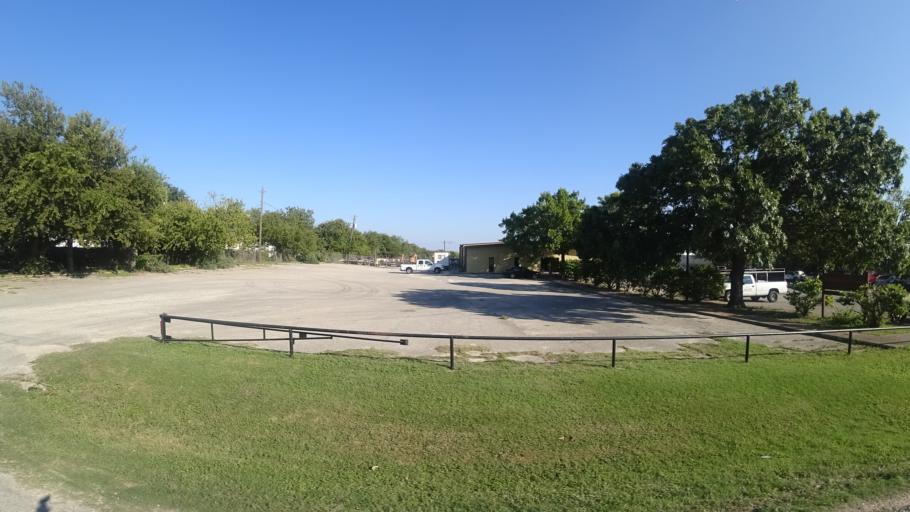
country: US
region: Texas
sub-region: Travis County
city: Wells Branch
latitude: 30.3513
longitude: -97.6693
